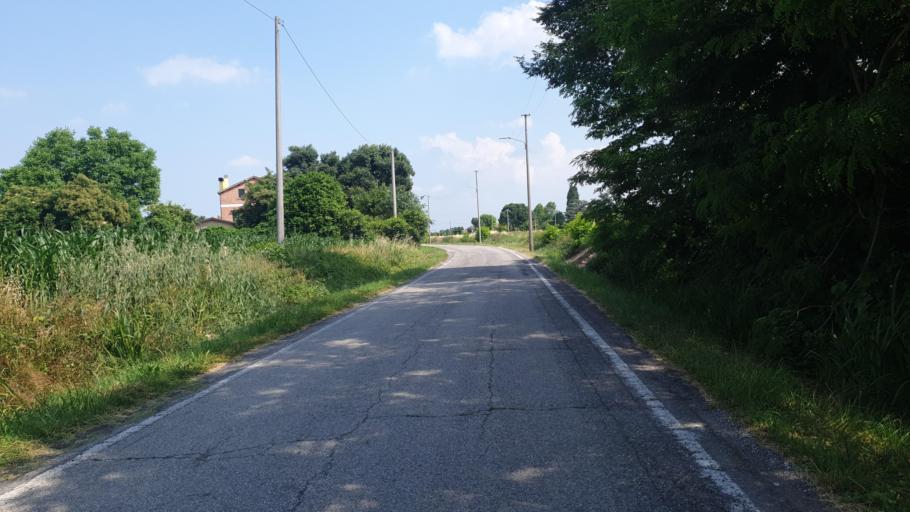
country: IT
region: Veneto
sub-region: Provincia di Padova
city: Tencarola
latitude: 45.3764
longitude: 11.8115
